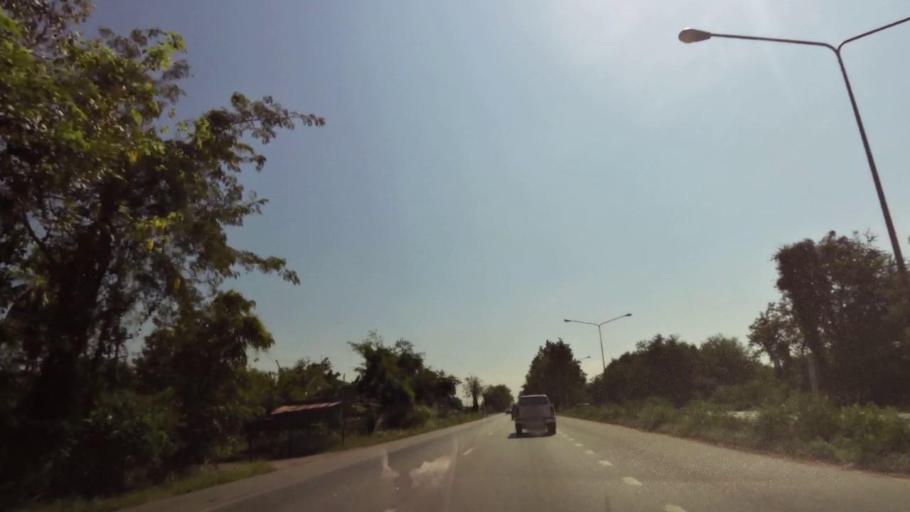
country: TH
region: Nakhon Sawan
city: Kao Liao
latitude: 15.8390
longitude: 100.1174
